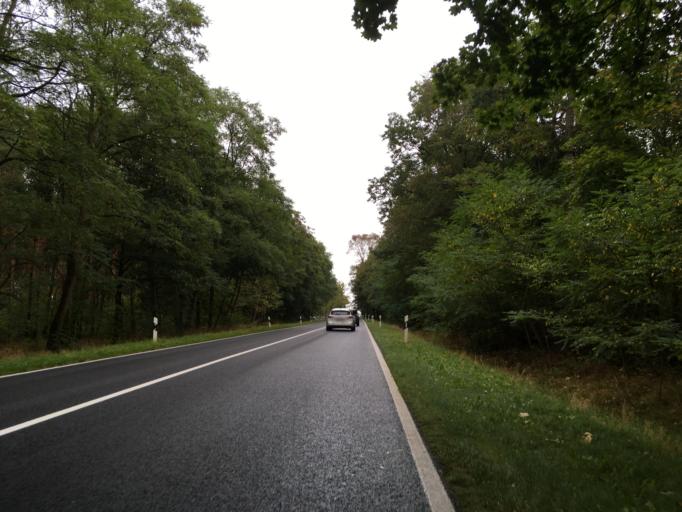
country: DE
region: Brandenburg
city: Werftpfuhl
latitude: 52.6903
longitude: 13.8600
